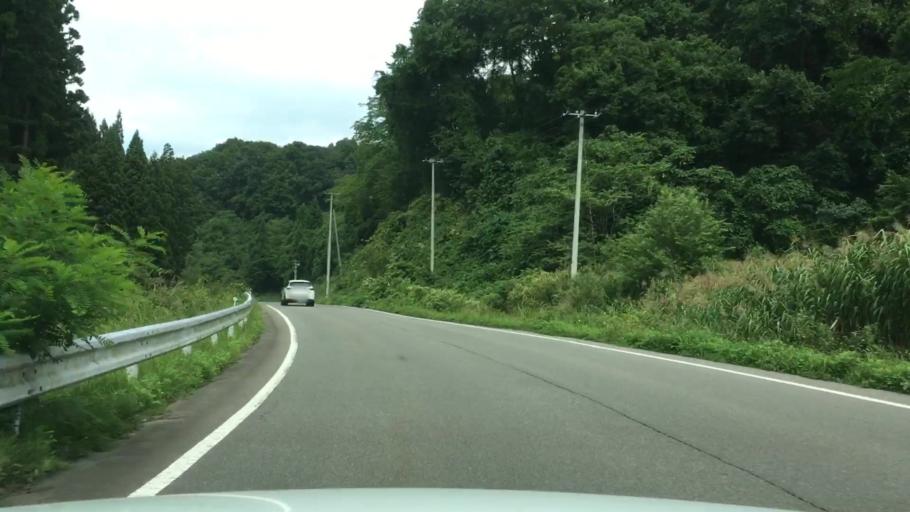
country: JP
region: Aomori
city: Shimokizukuri
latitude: 40.7316
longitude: 140.2520
